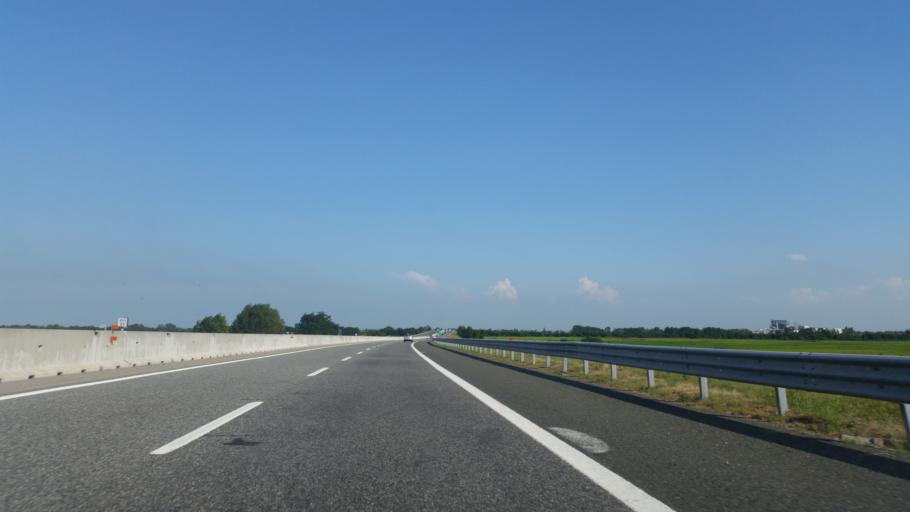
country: IT
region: Piedmont
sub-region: Provincia di Vercelli
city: Crova
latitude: 45.3441
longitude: 8.2050
